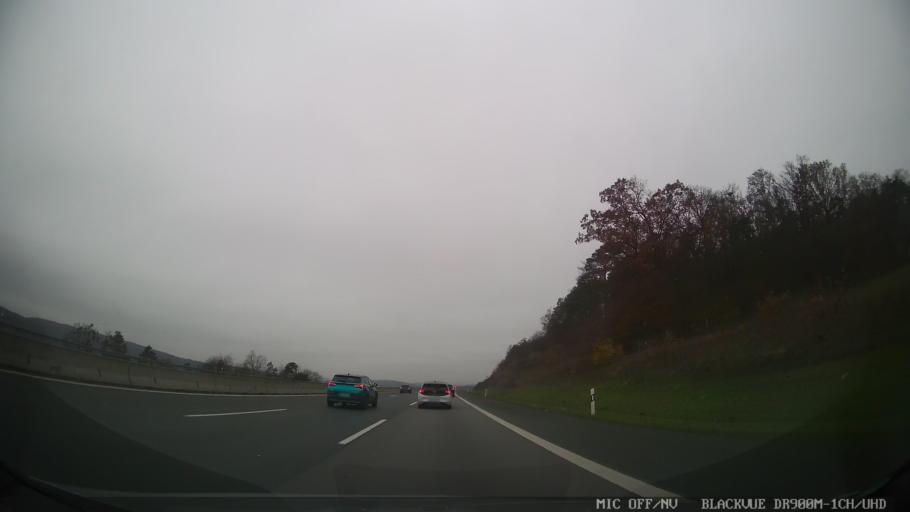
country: DE
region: Bavaria
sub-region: Regierungsbezirk Unterfranken
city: Holzkirchen
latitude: 49.7673
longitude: 9.6908
